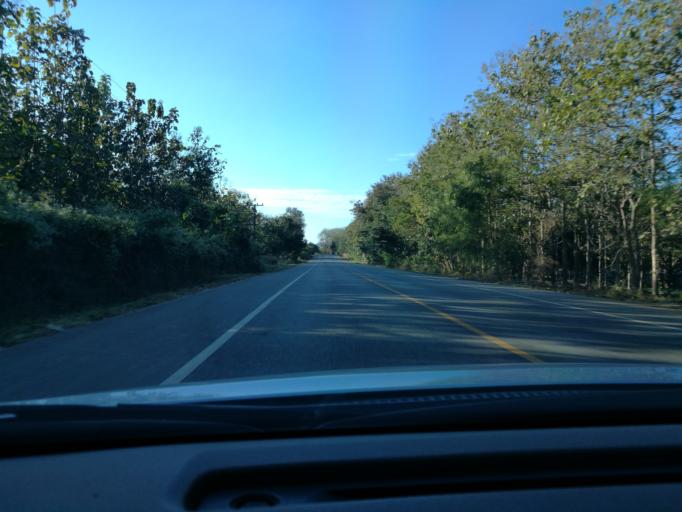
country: TH
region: Phitsanulok
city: Nakhon Thai
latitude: 17.0719
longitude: 100.8359
